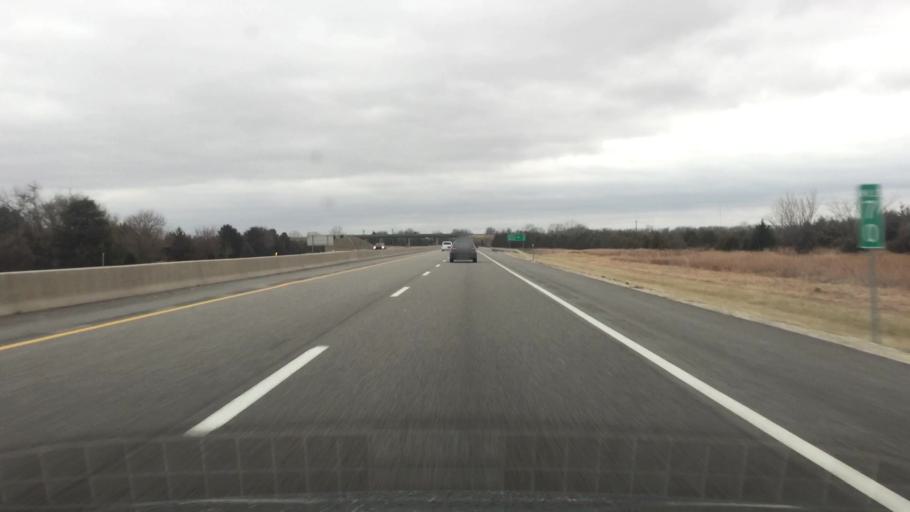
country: US
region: Kansas
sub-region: Butler County
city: El Dorado
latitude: 37.8135
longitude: -96.9109
